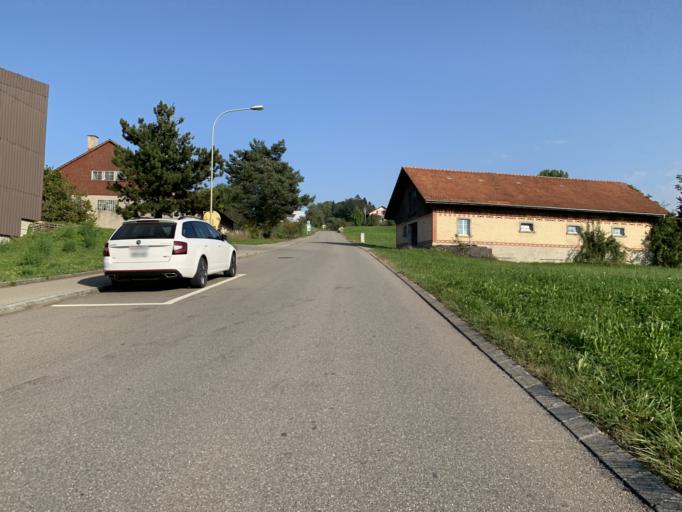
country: CH
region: Zurich
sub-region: Bezirk Hinwil
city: Baretswil
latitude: 47.3332
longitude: 8.8586
